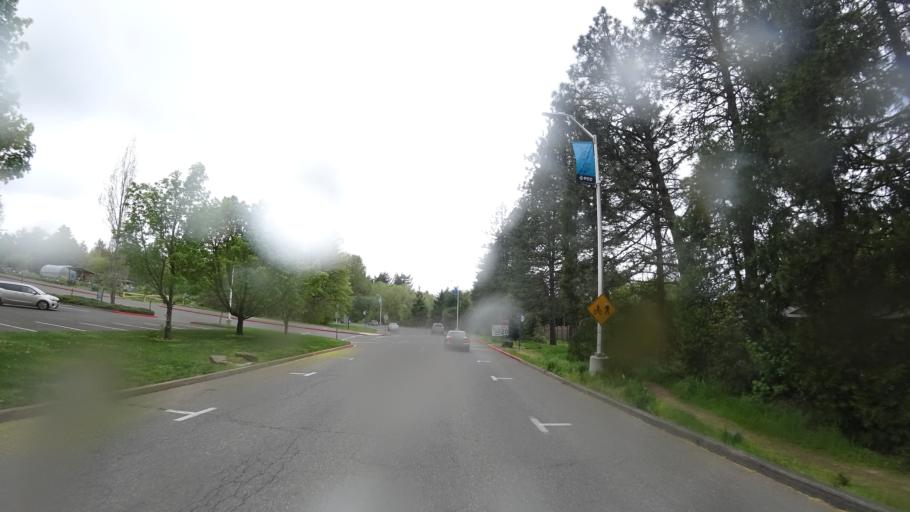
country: US
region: Oregon
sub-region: Washington County
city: Metzger
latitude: 45.4413
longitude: -122.7333
